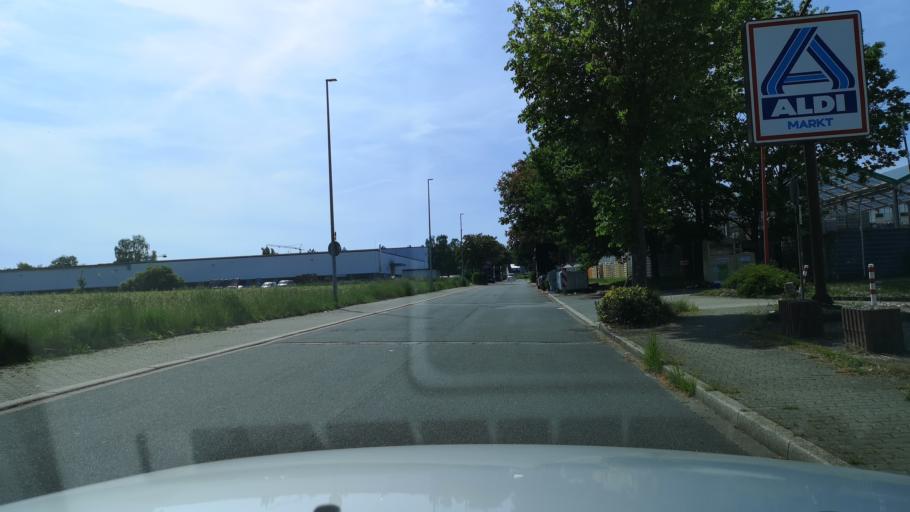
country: DE
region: North Rhine-Westphalia
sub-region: Regierungsbezirk Arnsberg
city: Menden
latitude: 51.4457
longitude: 7.7619
